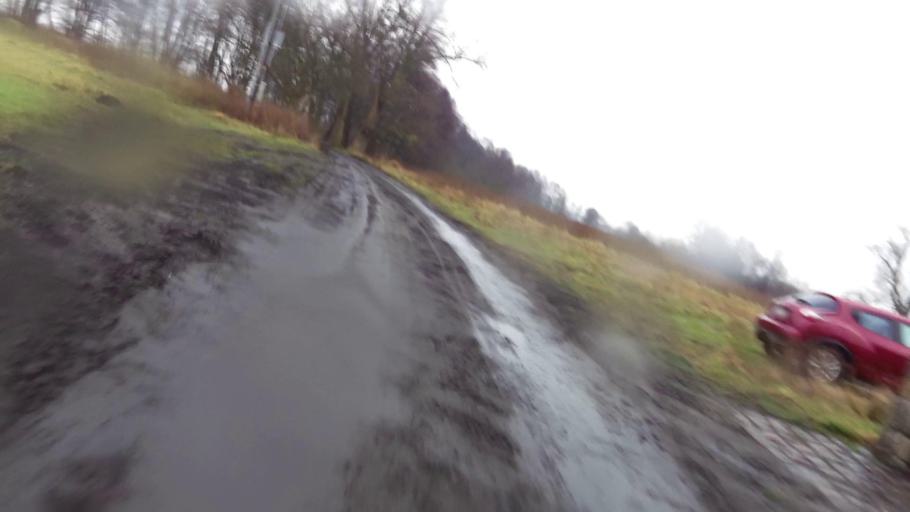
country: PL
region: West Pomeranian Voivodeship
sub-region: Szczecin
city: Szczecin
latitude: 53.4412
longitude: 14.7138
